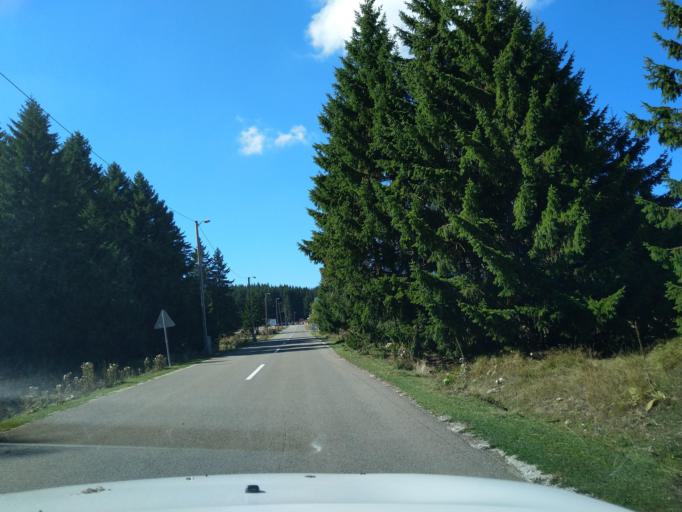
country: RS
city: Sokolovica
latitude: 43.2768
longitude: 20.3424
